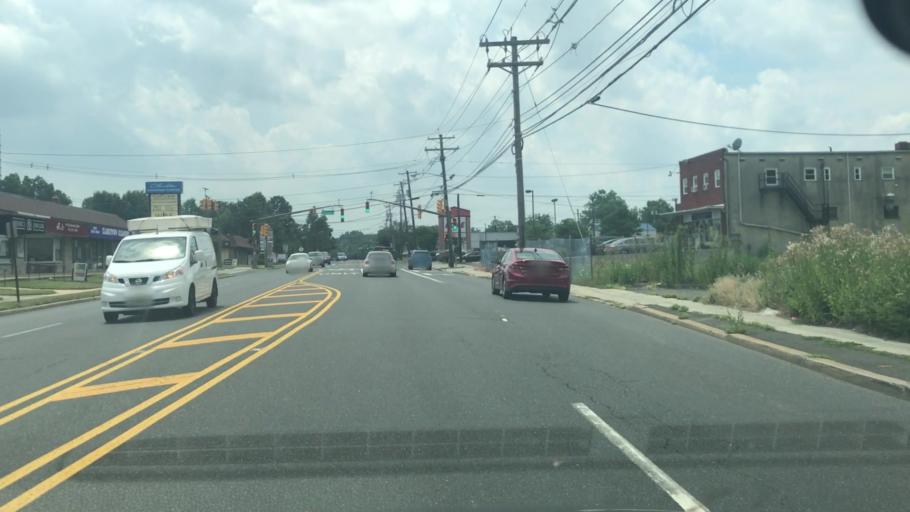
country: US
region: New Jersey
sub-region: Union County
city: Clark
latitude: 40.6284
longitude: -74.3144
